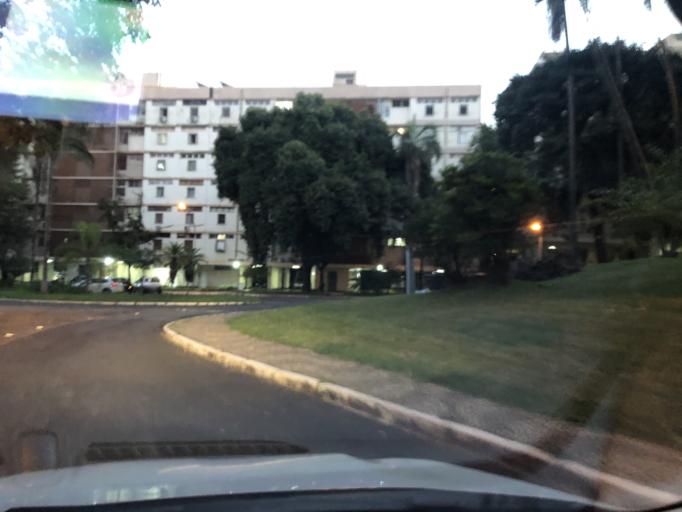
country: BR
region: Federal District
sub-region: Brasilia
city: Brasilia
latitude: -15.8089
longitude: -47.8985
